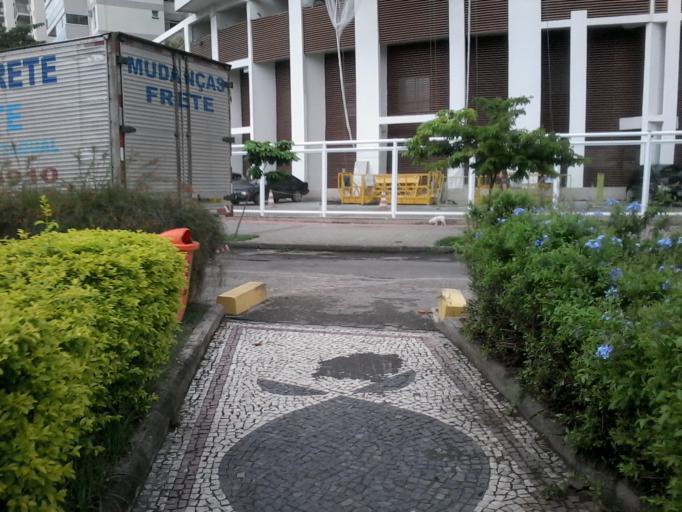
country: BR
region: Rio de Janeiro
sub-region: Nilopolis
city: Nilopolis
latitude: -23.0227
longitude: -43.4872
